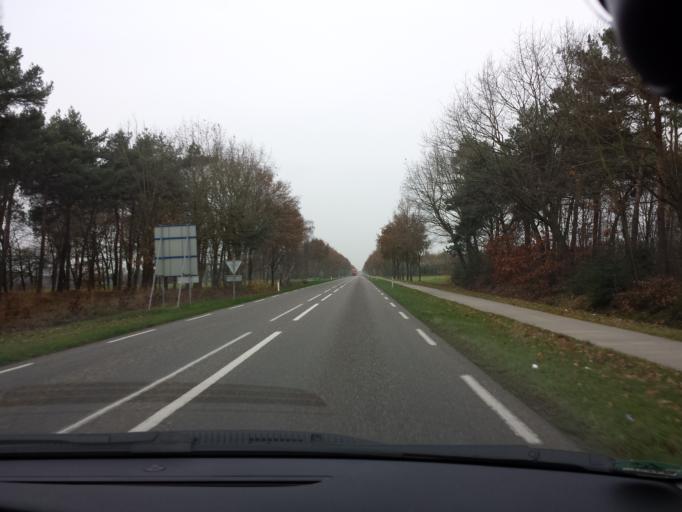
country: NL
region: Limburg
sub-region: Gemeente Peel en Maas
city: Maasbree
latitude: 51.3943
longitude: 5.9735
